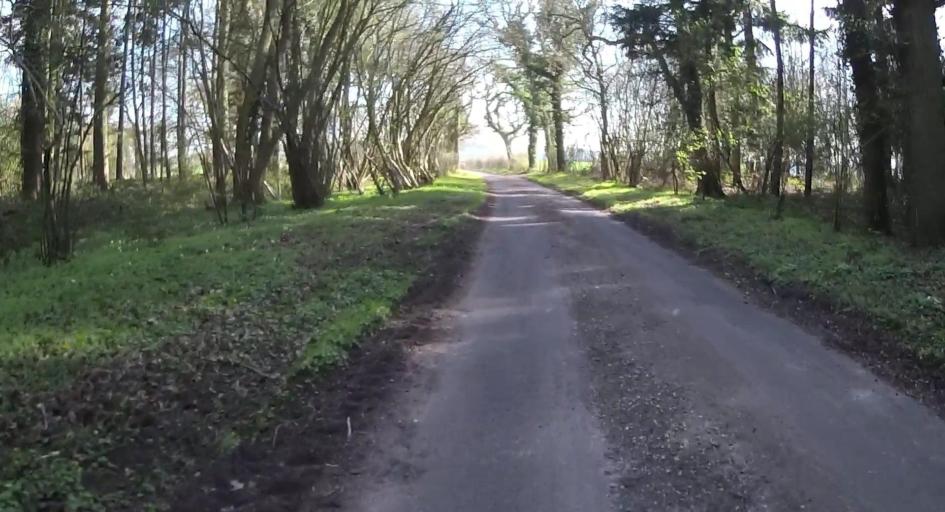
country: GB
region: England
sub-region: Hampshire
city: Highclere
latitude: 51.2537
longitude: -1.3675
